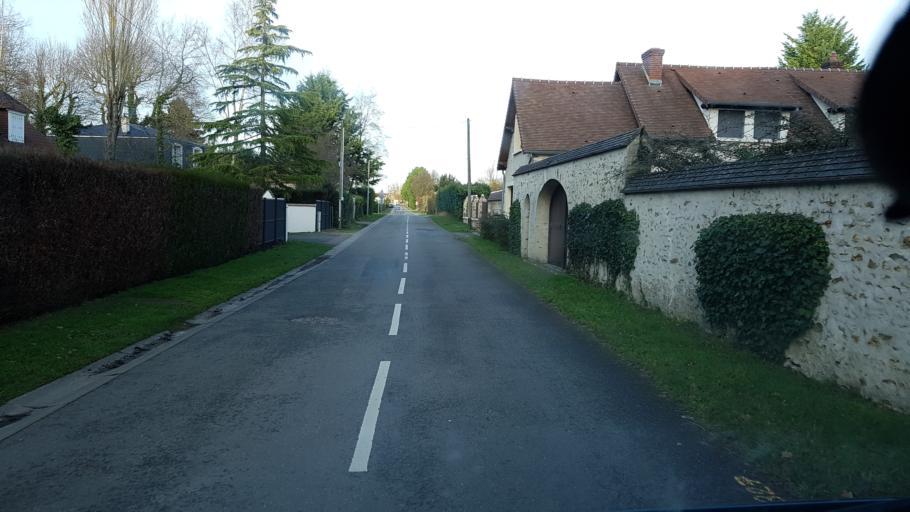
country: FR
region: Ile-de-France
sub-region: Departement des Yvelines
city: Saint-Leger-en-Yvelines
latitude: 48.6999
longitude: 1.8087
